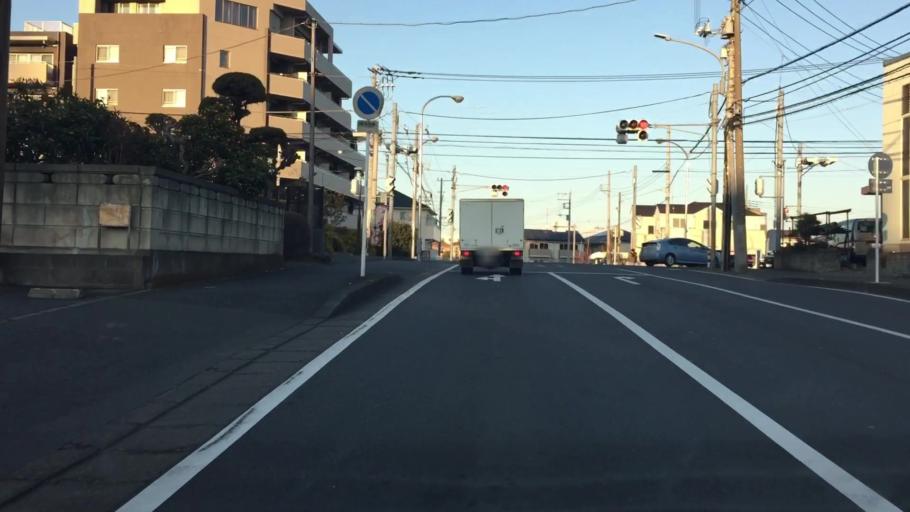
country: JP
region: Ibaraki
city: Moriya
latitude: 35.9111
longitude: 139.9504
